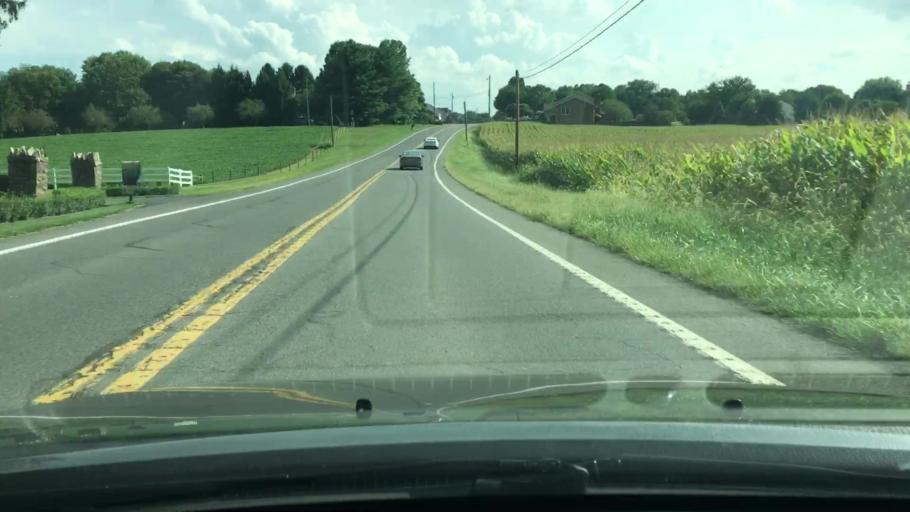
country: US
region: Pennsylvania
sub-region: Franklin County
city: Guilford
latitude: 39.9309
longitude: -77.5905
